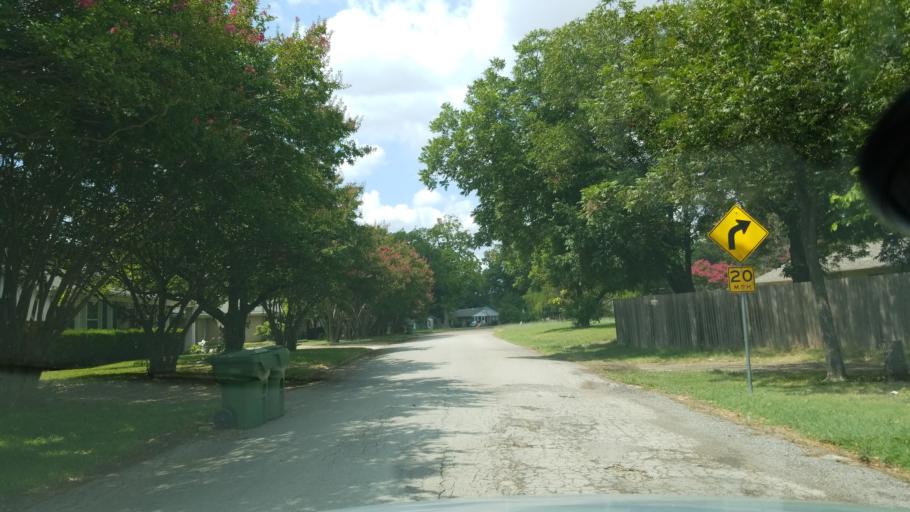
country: US
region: Texas
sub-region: Dallas County
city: Garland
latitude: 32.9175
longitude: -96.6543
